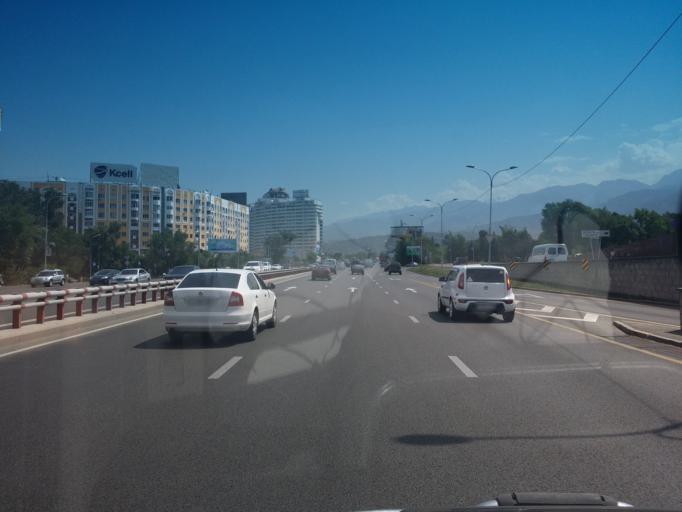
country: KZ
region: Almaty Qalasy
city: Almaty
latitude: 43.1947
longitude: 76.8865
